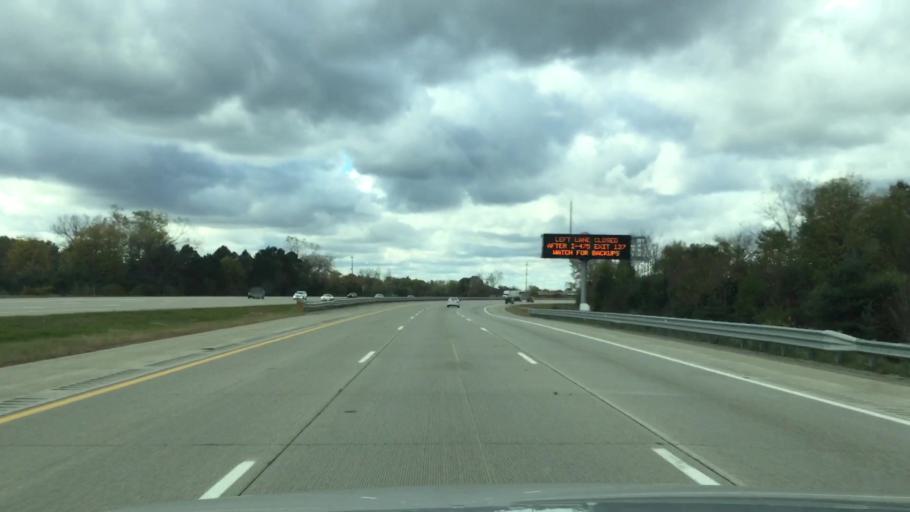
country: US
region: Michigan
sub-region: Genesee County
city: Burton
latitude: 43.0156
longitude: -83.6215
